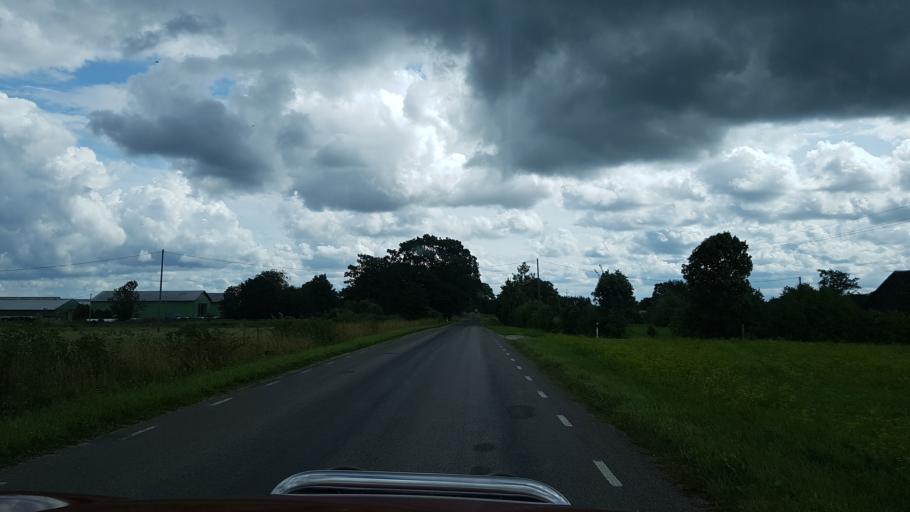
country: EE
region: Laeaene
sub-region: Lihula vald
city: Lihula
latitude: 58.7127
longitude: 24.0052
